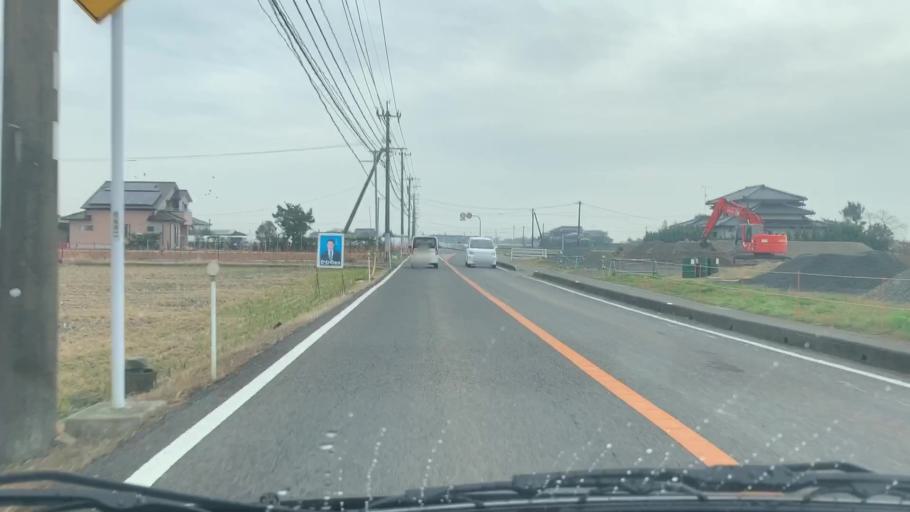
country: JP
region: Saga Prefecture
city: Kashima
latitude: 33.1850
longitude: 130.1567
